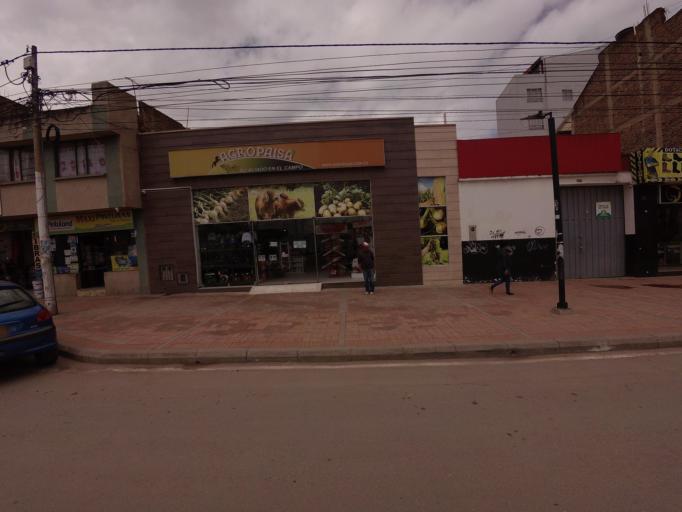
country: CO
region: Boyaca
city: Sogamoso
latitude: 5.7169
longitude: -72.9326
